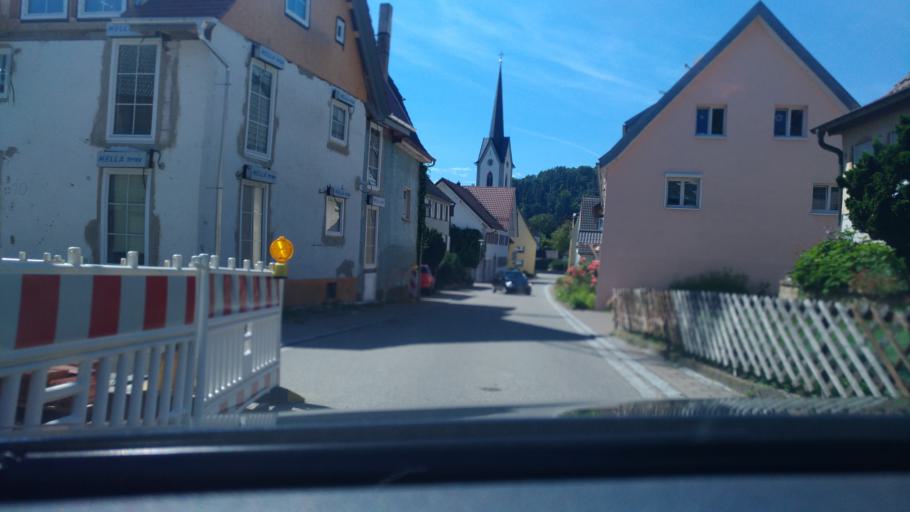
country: DE
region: Baden-Wuerttemberg
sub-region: Freiburg Region
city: Bodman-Ludwigshafen
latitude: 47.8191
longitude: 9.0615
